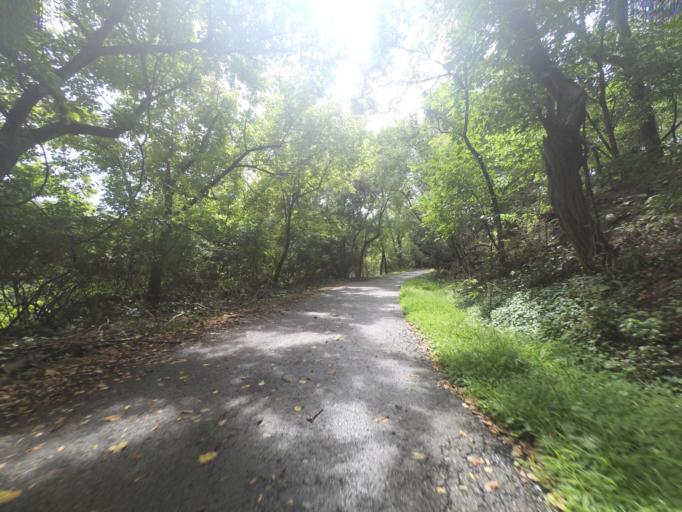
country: US
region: West Virginia
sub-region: Cabell County
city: Huntington
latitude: 38.4016
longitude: -82.4716
